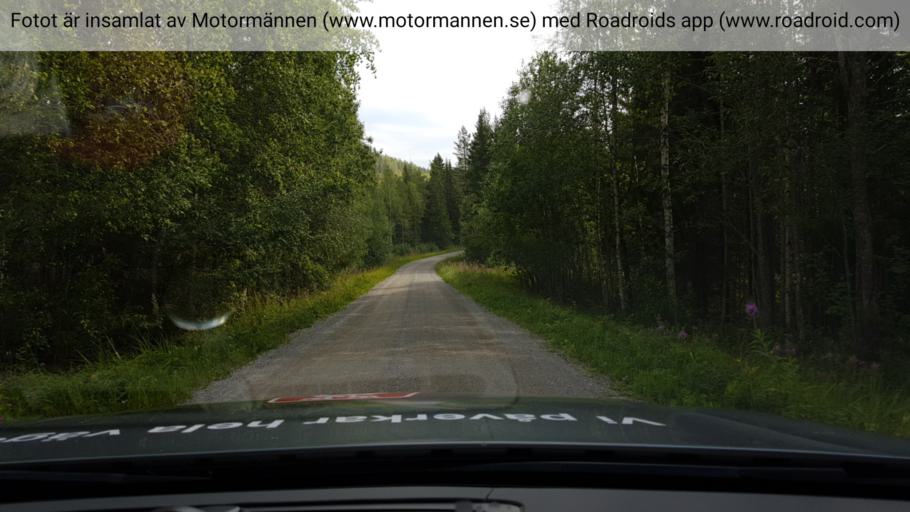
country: SE
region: Jaemtland
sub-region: OEstersunds Kommun
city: Brunflo
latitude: 63.0329
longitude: 15.0848
